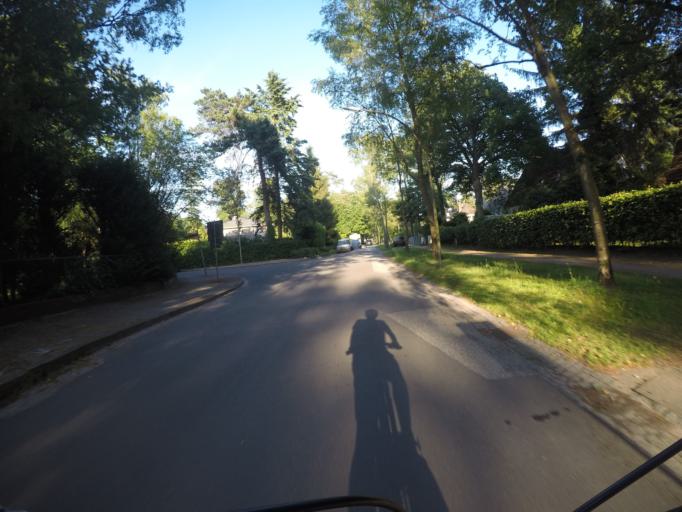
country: DE
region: Schleswig-Holstein
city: Wedel
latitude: 53.5862
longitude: 9.7471
